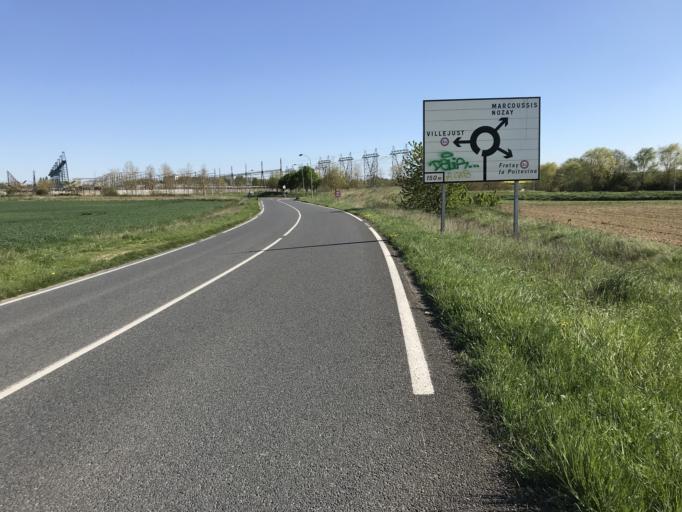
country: FR
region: Ile-de-France
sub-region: Departement de l'Essonne
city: Villejust
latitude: 48.6771
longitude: 2.2251
